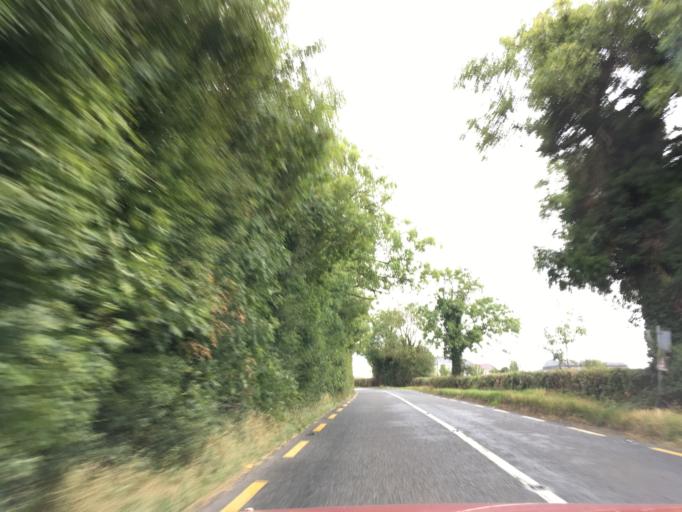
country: IE
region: Munster
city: Fethard
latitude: 52.4282
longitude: -7.7774
